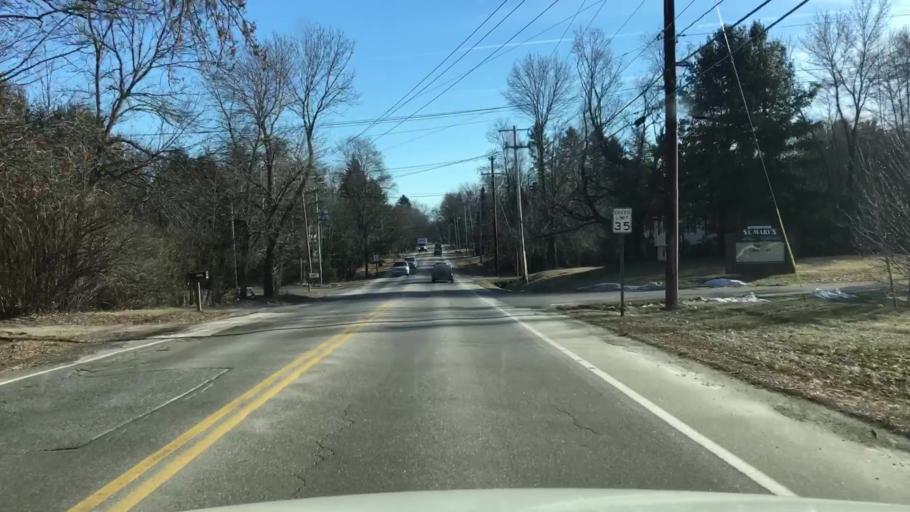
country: US
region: Maine
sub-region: Penobscot County
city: Bangor
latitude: 44.8171
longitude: -68.8000
